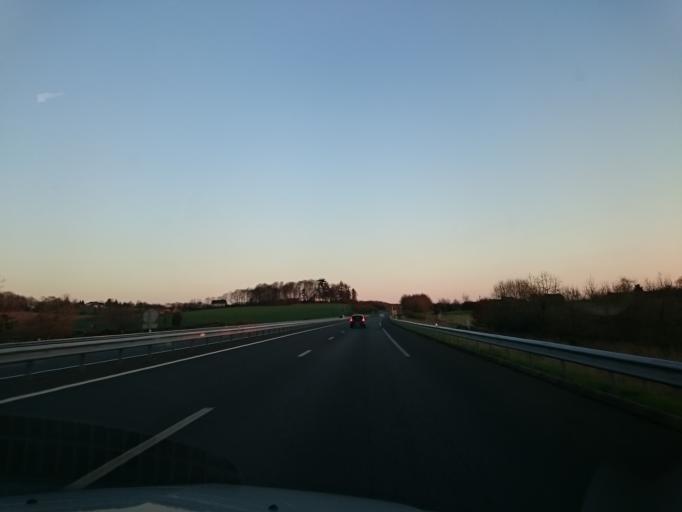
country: FR
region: Brittany
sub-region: Departement d'Ille-et-Vilaine
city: Saint-Etienne-en-Cogles
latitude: 48.4043
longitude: -1.3109
